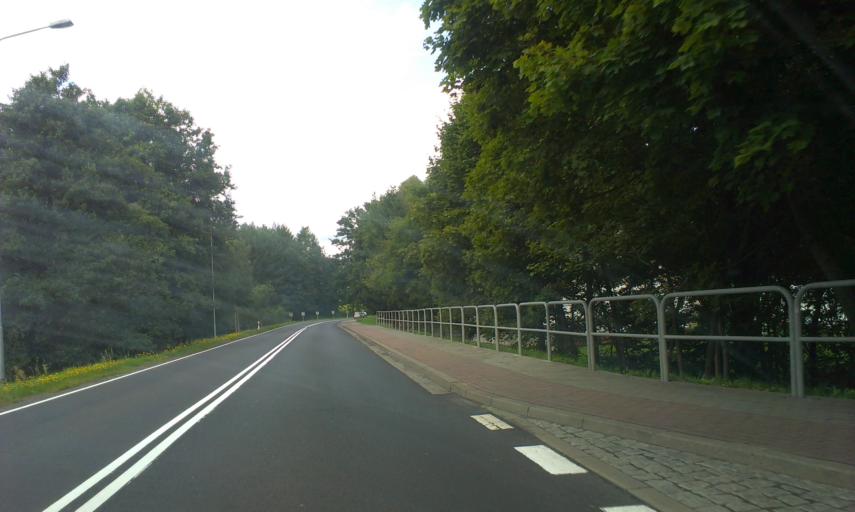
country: PL
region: West Pomeranian Voivodeship
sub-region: Powiat koszalinski
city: Bobolice
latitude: 54.0019
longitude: 16.5202
